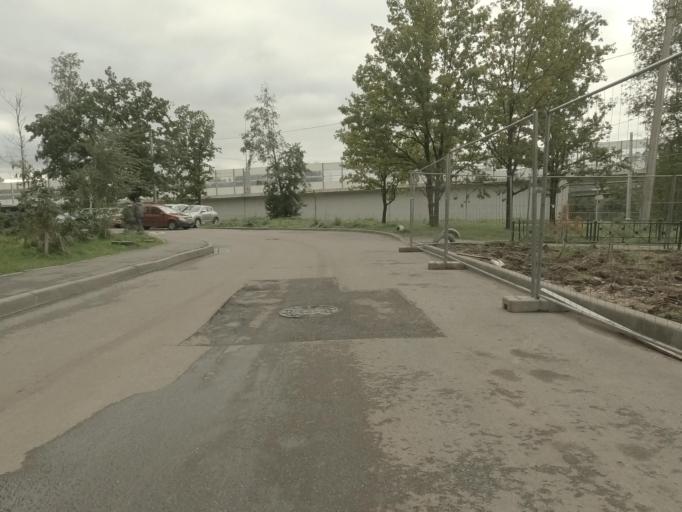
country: RU
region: St.-Petersburg
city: Krasnogvargeisky
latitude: 59.9798
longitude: 30.5077
